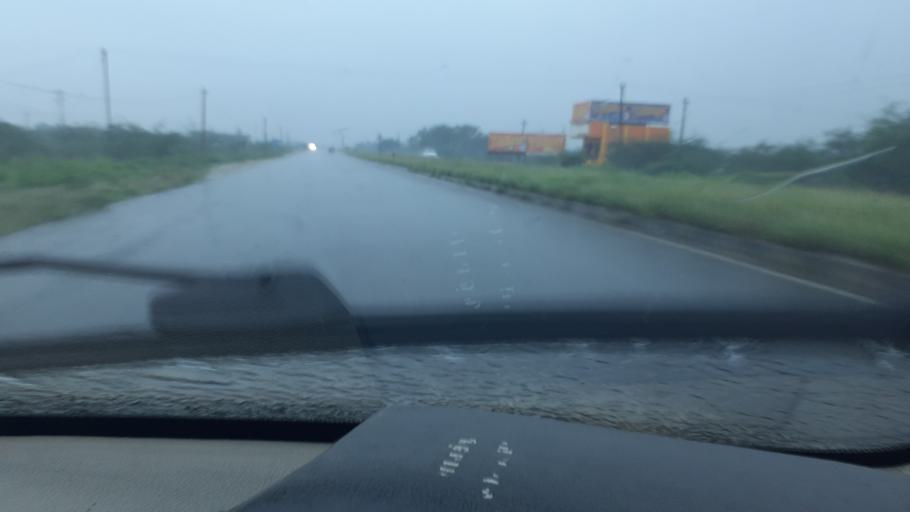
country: IN
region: Tamil Nadu
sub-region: Virudhunagar
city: Sattur
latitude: 9.4273
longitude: 77.9185
